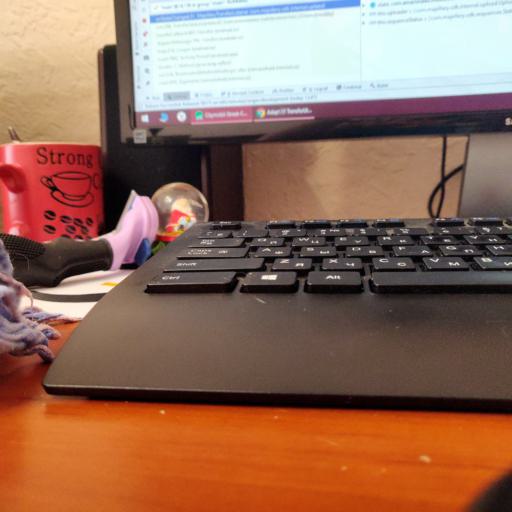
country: FI
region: Haeme
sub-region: Forssa
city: Humppila
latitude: 60.8872
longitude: 23.4324
